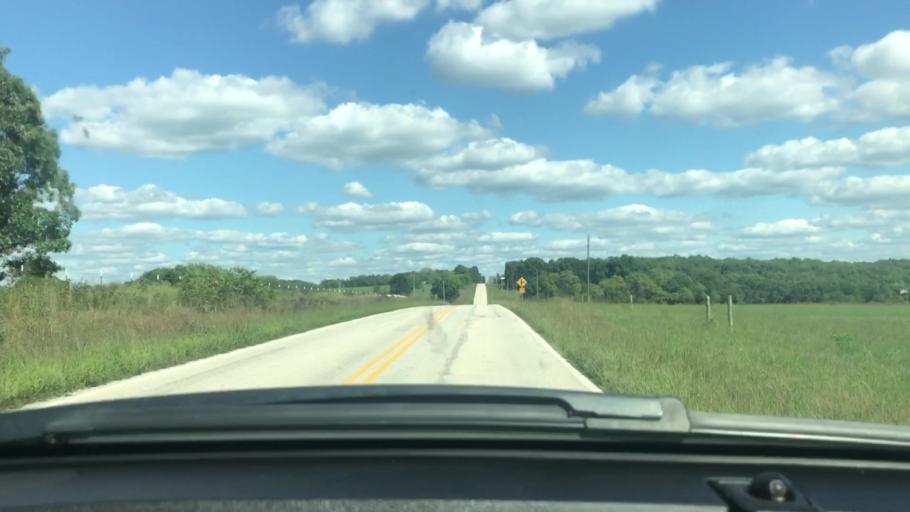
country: US
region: Missouri
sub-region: Wright County
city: Hartville
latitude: 37.3769
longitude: -92.4176
